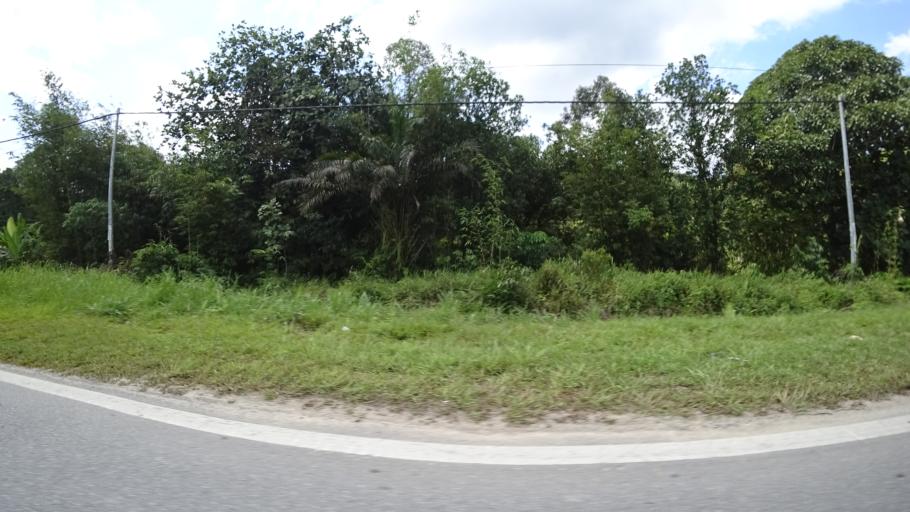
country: MY
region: Sarawak
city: Limbang
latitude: 4.6573
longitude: 114.9559
